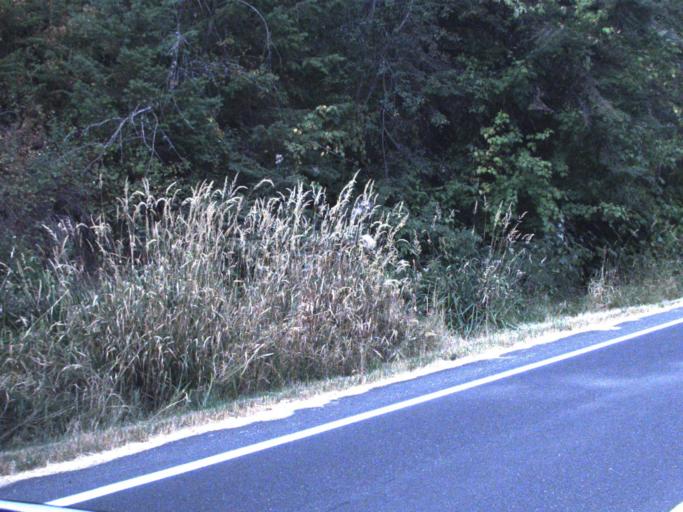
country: US
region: Washington
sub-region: Spokane County
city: Otis Orchards-East Farms
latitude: 47.8814
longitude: -117.1361
